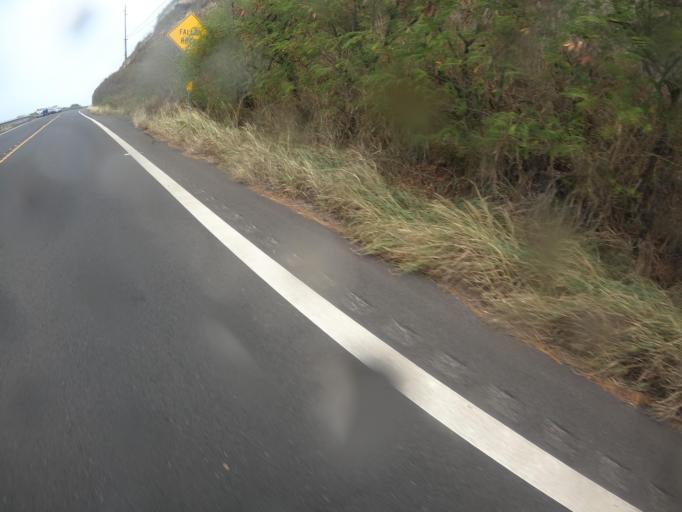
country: US
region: Hawaii
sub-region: Honolulu County
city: Makaha Valley
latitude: 21.5410
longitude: -158.2354
